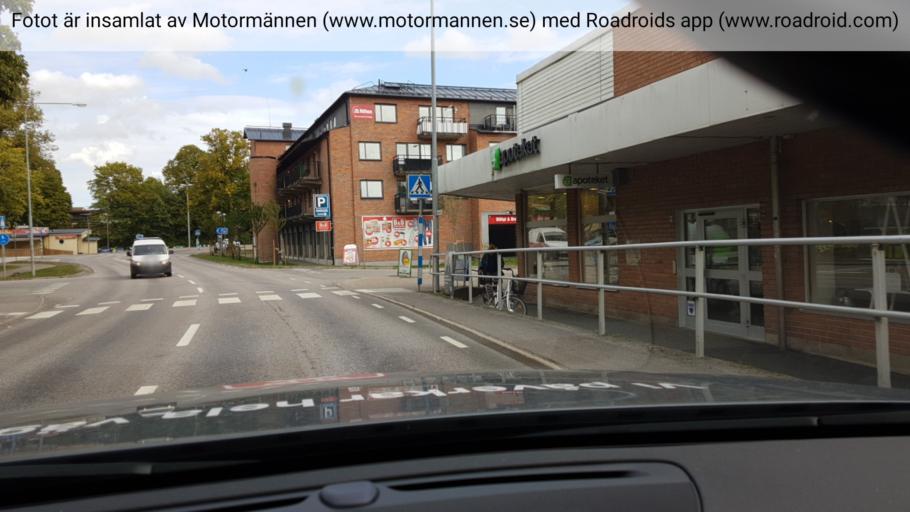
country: SE
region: Stockholm
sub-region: Norrtalje Kommun
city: Rimbo
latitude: 59.7437
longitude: 18.3656
